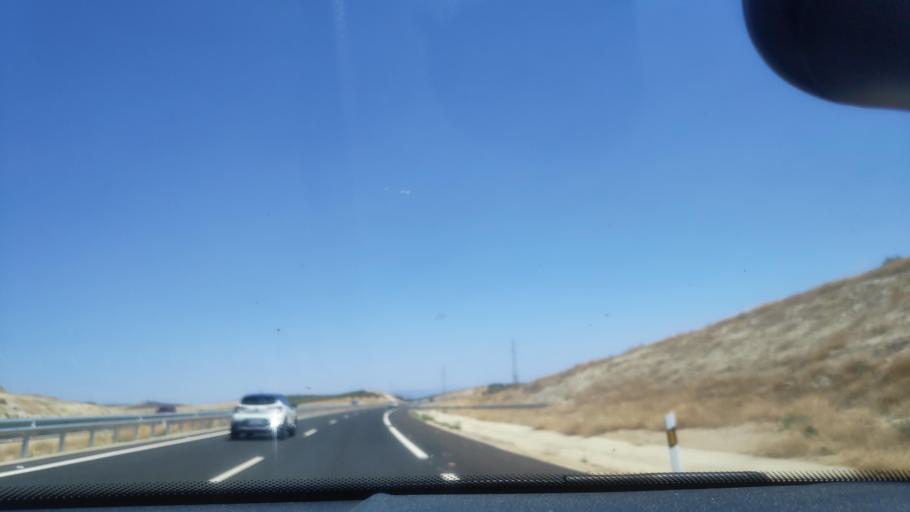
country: ES
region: Andalusia
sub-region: Provincia de Granada
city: Otura
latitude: 37.0777
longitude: -3.6633
